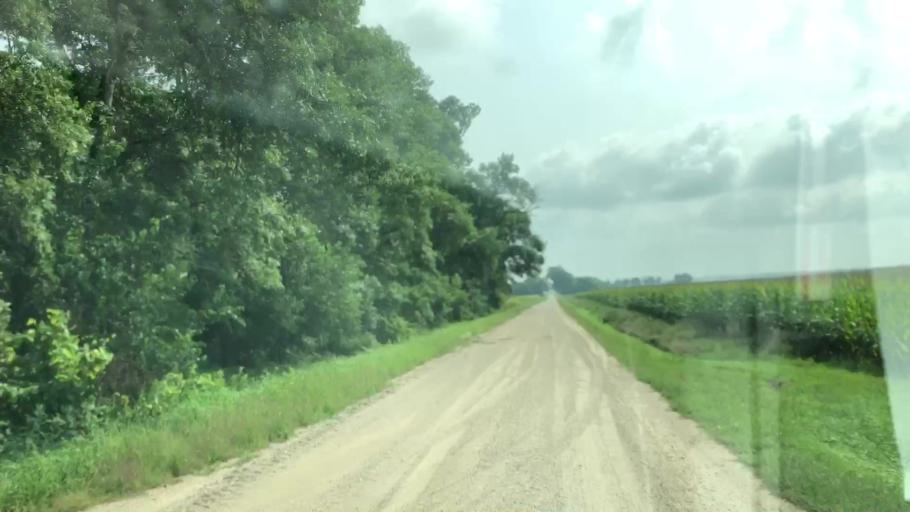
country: US
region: Iowa
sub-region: O'Brien County
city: Sheldon
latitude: 43.2004
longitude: -95.8978
